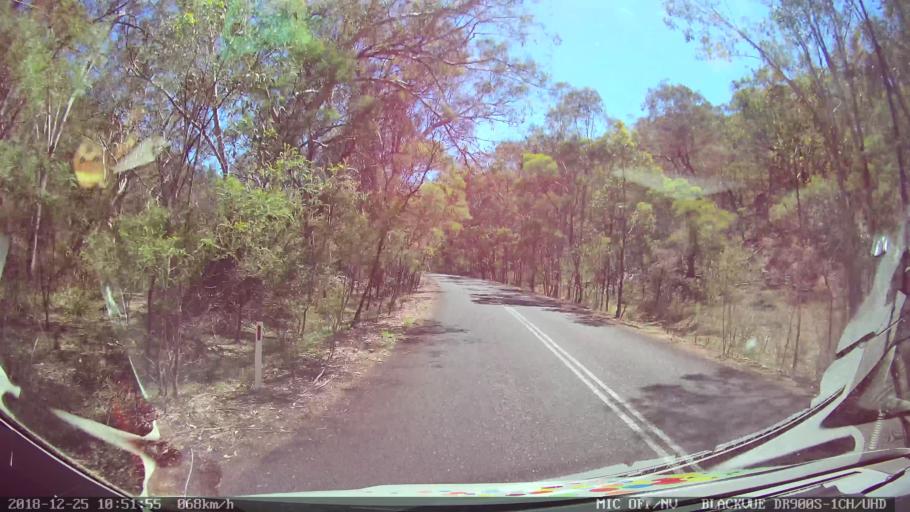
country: AU
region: New South Wales
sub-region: Upper Hunter Shire
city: Merriwa
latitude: -32.4332
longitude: 150.2720
